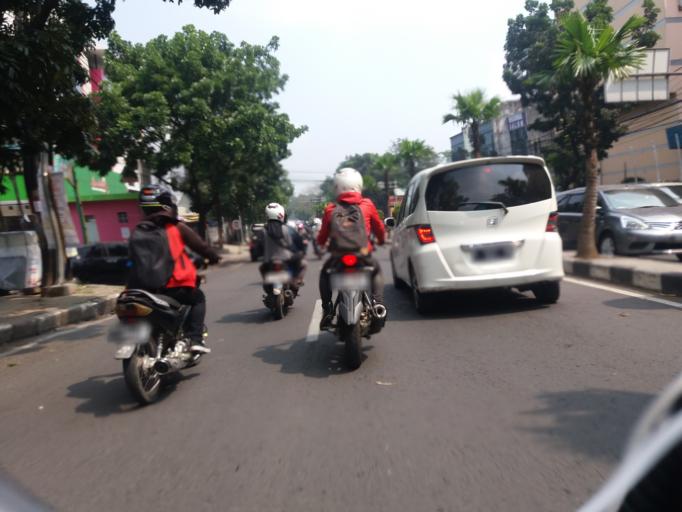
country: ID
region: West Java
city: Bandung
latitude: -6.9065
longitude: 107.5970
